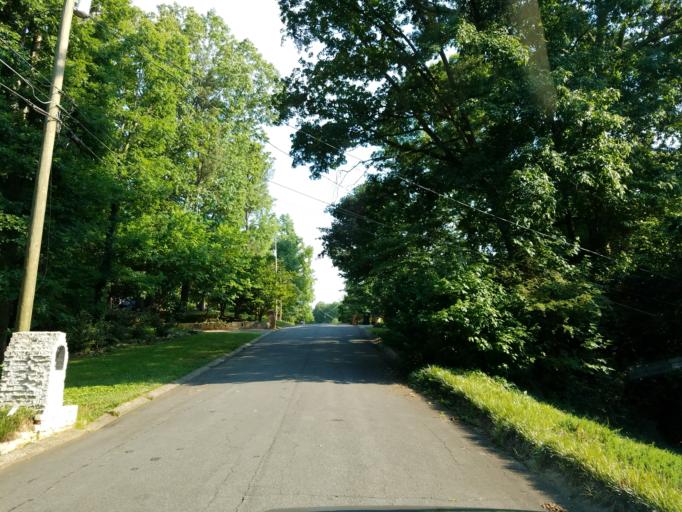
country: US
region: Georgia
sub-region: Cobb County
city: Vinings
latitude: 33.9184
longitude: -84.4719
